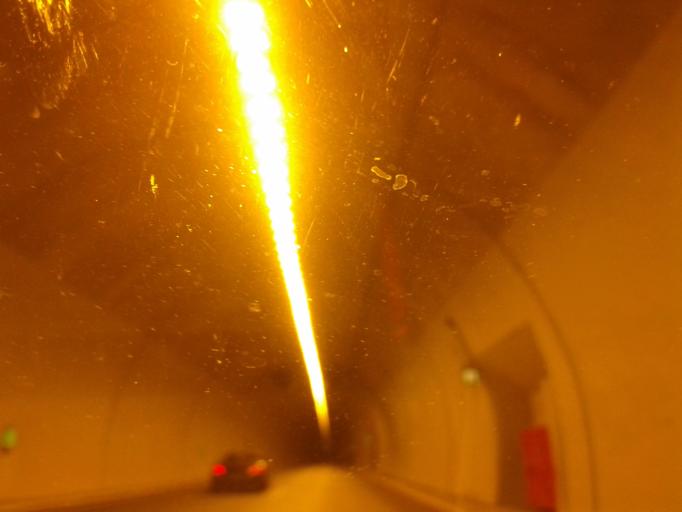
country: GR
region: West Greece
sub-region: Nomos Achaias
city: Aiyira
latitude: 38.1398
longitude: 22.3766
